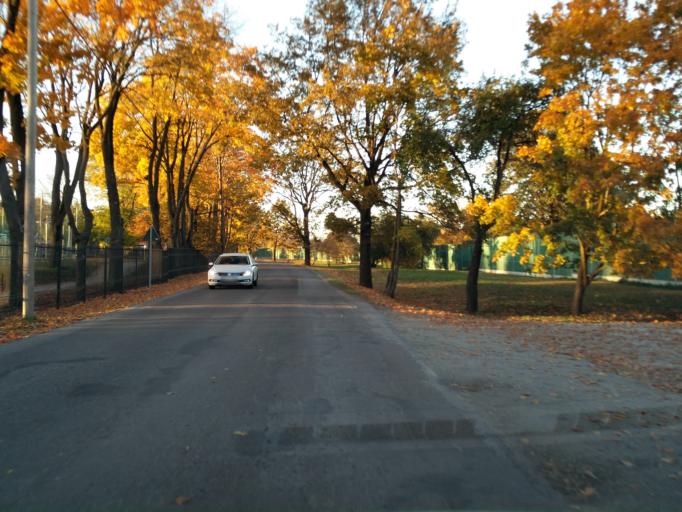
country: EE
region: Tartu
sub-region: Tartu linn
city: Tartu
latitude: 58.3652
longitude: 26.7165
